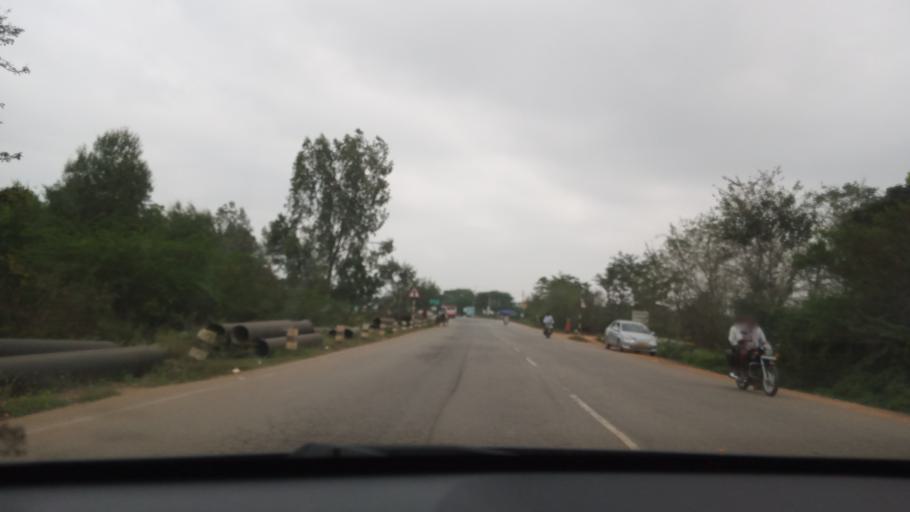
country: IN
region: Karnataka
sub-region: Bangalore Rural
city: Vijayapura
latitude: 13.2497
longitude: 77.9368
